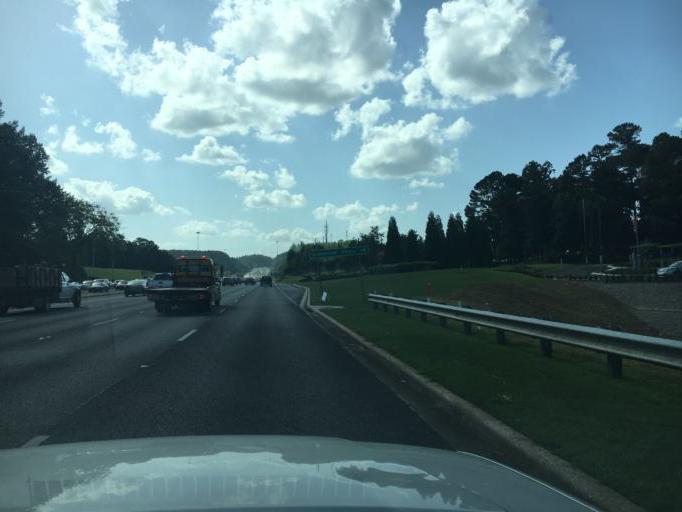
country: US
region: Alabama
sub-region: Jefferson County
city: Cahaba Heights
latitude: 33.4377
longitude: -86.7224
